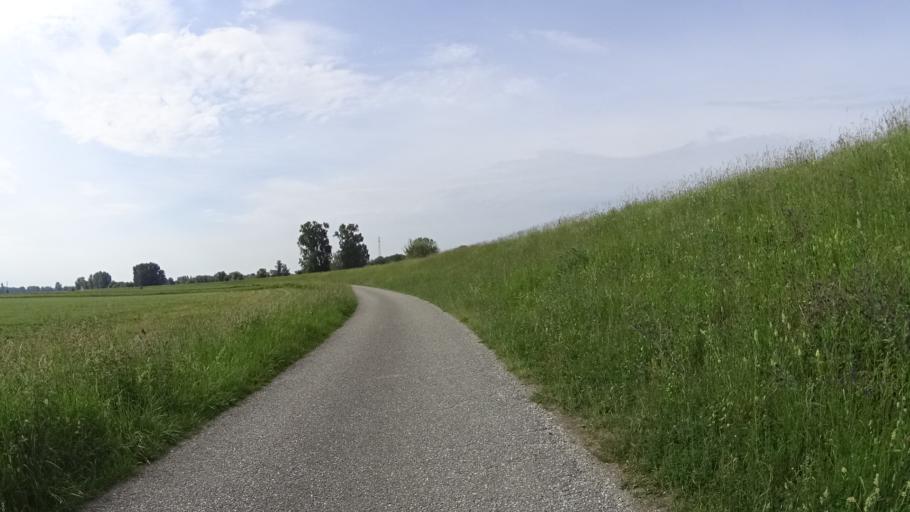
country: DE
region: Bavaria
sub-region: Lower Bavaria
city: Irlbach
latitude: 48.8450
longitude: 12.7674
